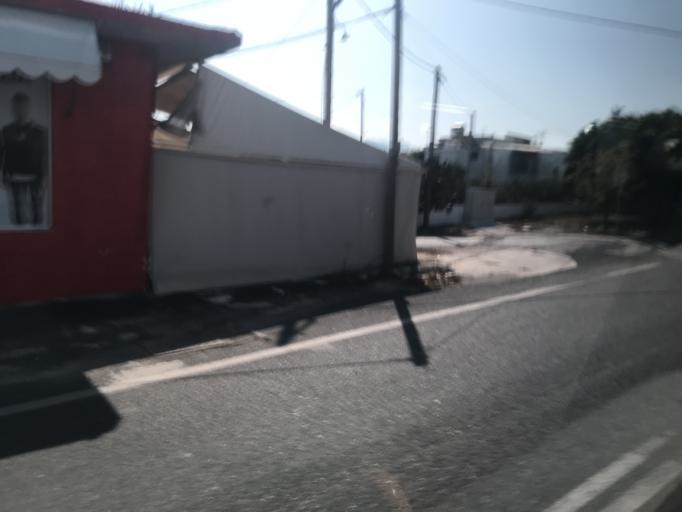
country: GR
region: Crete
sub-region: Nomos Irakleiou
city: Gazi
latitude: 35.3140
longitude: 25.0918
